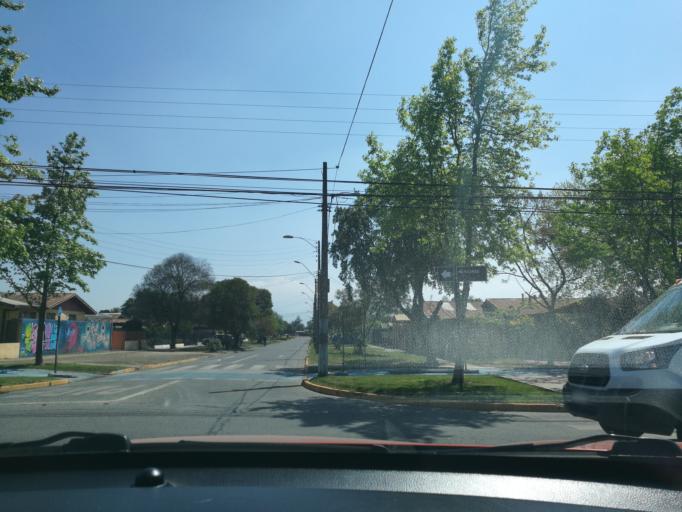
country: CL
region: O'Higgins
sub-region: Provincia de Cachapoal
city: Rancagua
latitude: -34.1582
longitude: -70.7325
